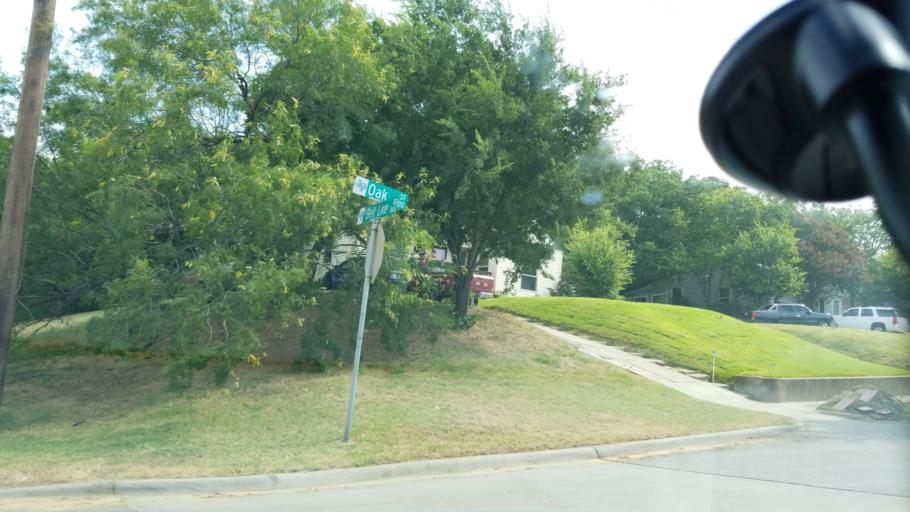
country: US
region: Texas
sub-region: Dallas County
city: Grand Prairie
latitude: 32.7508
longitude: -96.9946
